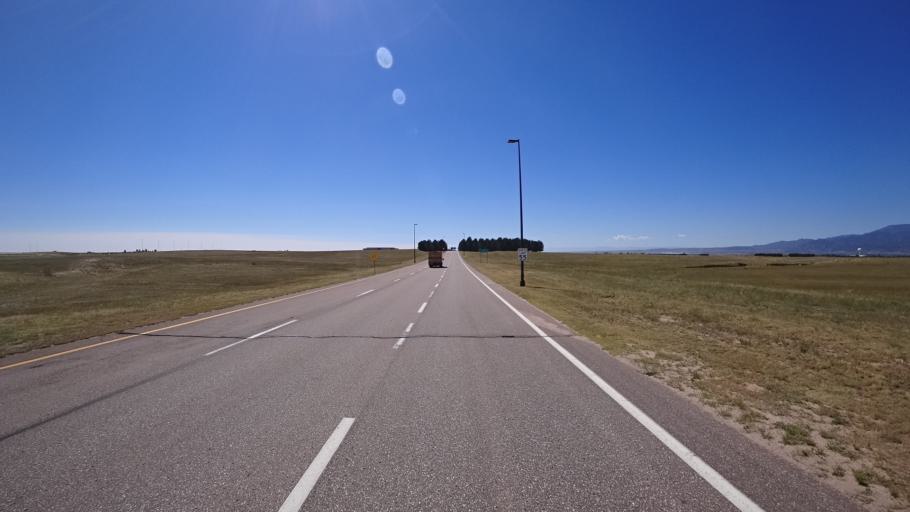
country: US
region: Colorado
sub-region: El Paso County
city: Security-Widefield
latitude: 38.7890
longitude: -104.7043
